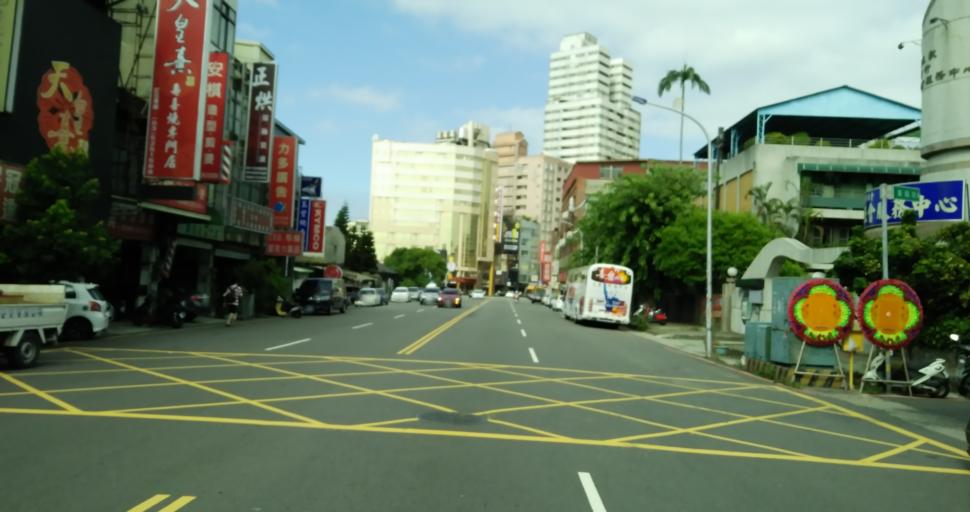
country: TW
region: Taiwan
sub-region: Hsinchu
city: Hsinchu
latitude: 24.8039
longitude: 120.9607
